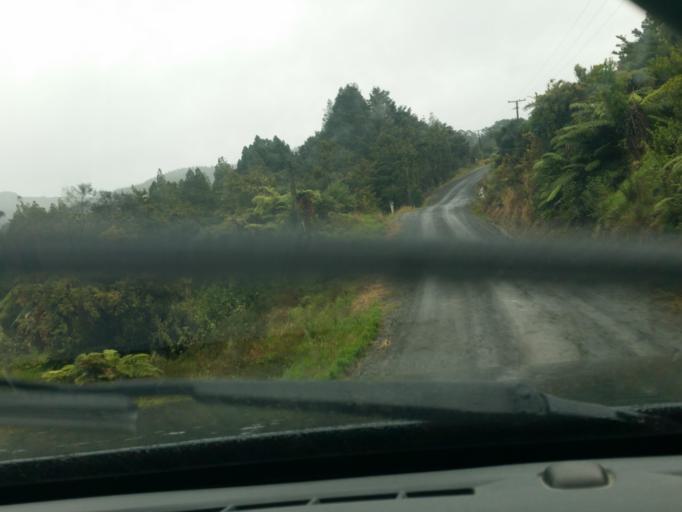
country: NZ
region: Northland
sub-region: Kaipara District
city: Dargaville
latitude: -35.7656
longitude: 173.6996
